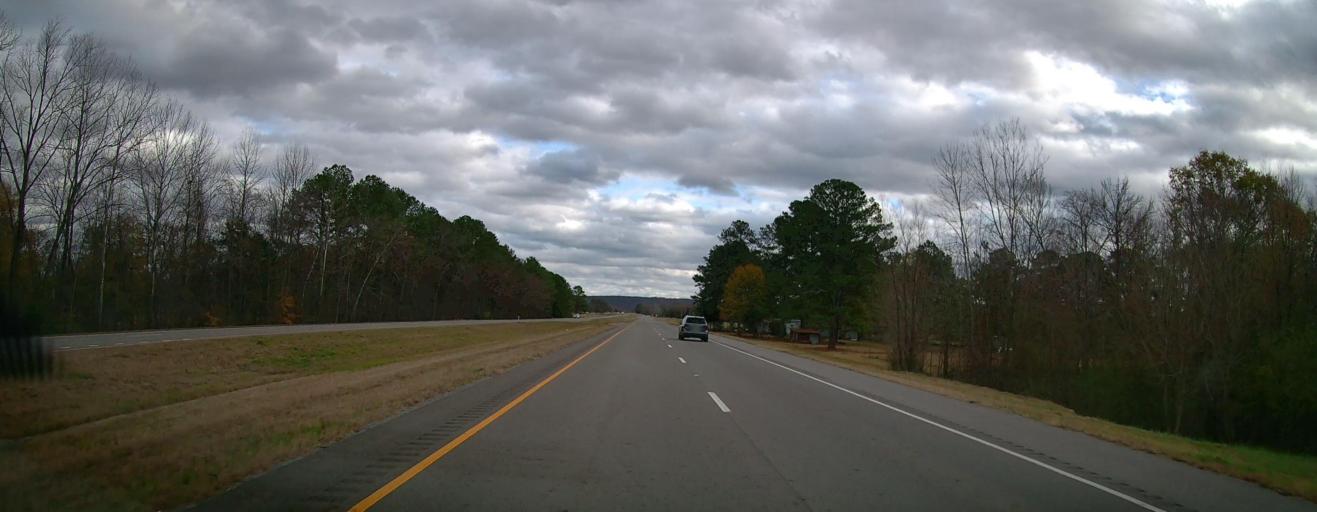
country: US
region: Alabama
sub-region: Morgan County
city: Danville
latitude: 34.3486
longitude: -87.0405
